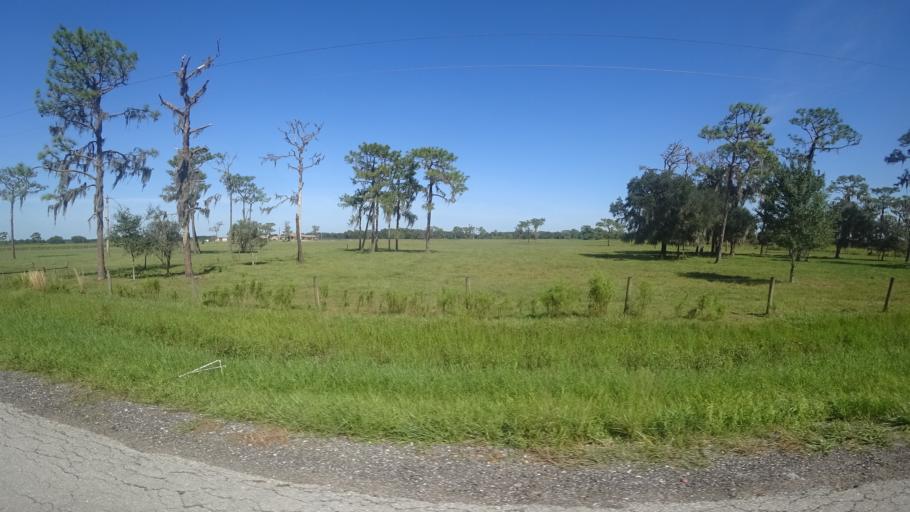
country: US
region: Florida
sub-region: Sarasota County
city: Warm Mineral Springs
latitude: 27.2736
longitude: -82.1577
